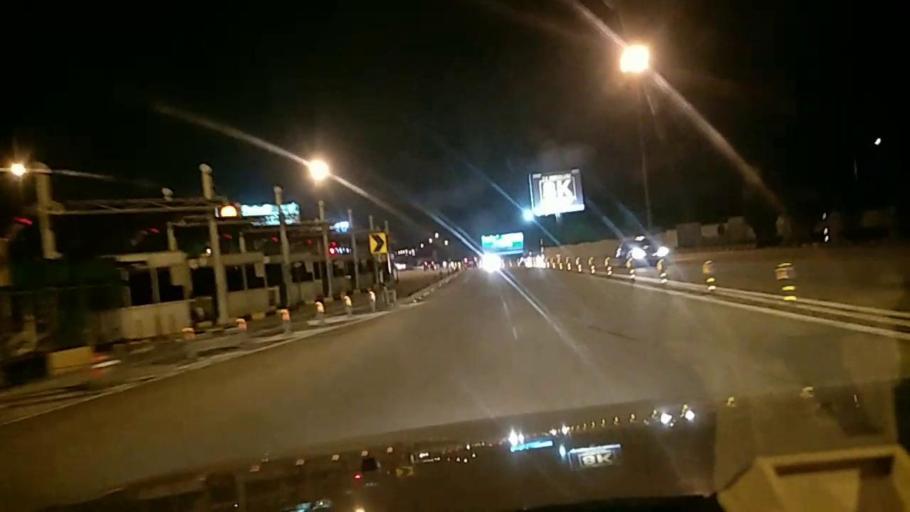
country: MY
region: Penang
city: Juru
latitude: 5.3245
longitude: 100.4365
